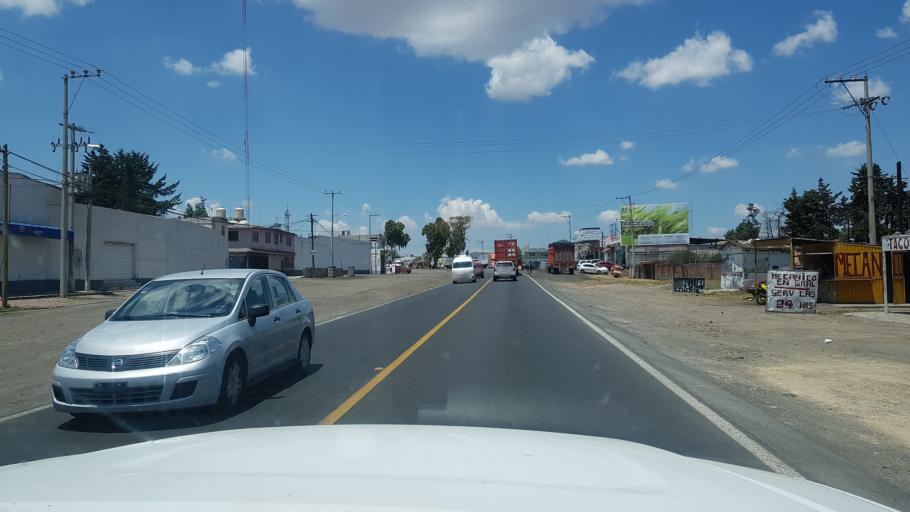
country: MX
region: Hidalgo
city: Calpulalpan
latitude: 19.5912
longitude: -98.5593
